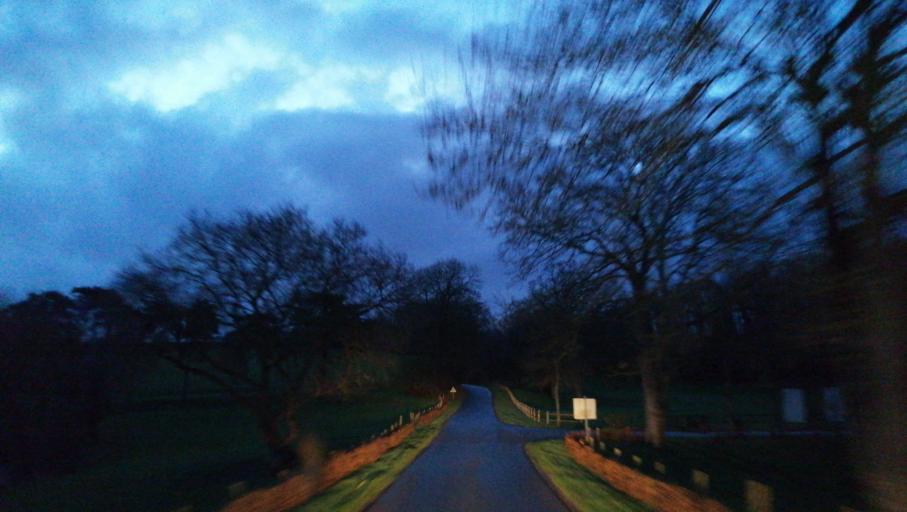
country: FR
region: Brittany
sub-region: Departement des Cotes-d'Armor
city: Plelo
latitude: 48.5587
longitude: -2.9601
